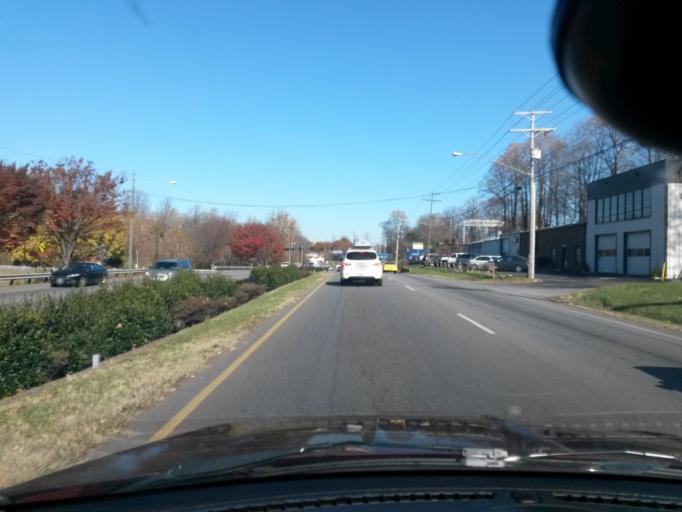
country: US
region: Virginia
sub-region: City of Lynchburg
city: West Lynchburg
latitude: 37.3542
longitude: -79.1827
